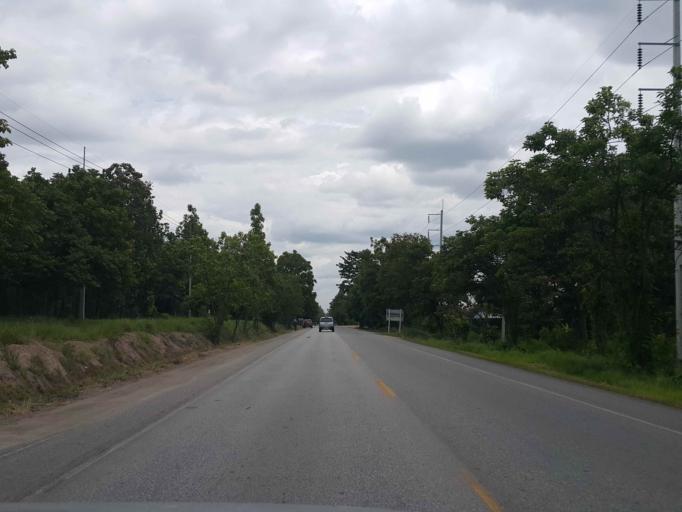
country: TH
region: Chiang Mai
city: Doi Lo
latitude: 18.4178
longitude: 98.8539
